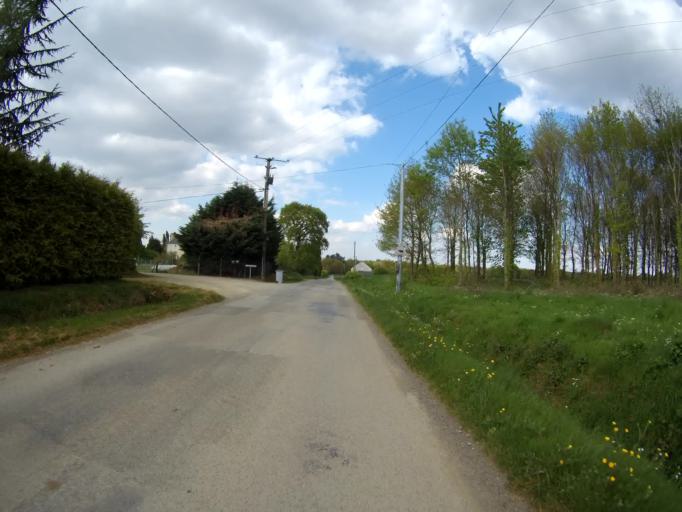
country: FR
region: Brittany
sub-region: Departement d'Ille-et-Vilaine
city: Vern-sur-Seiche
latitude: 48.0658
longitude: -1.5864
